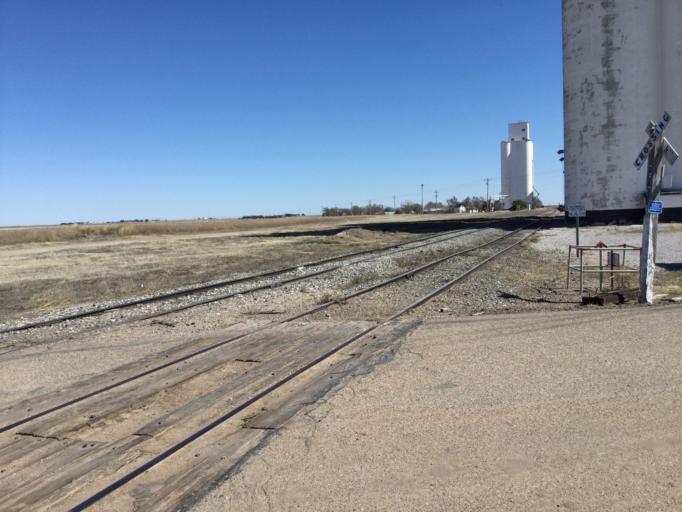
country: US
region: Kansas
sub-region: Grant County
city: Ulysses
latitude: 37.5630
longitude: -101.2358
